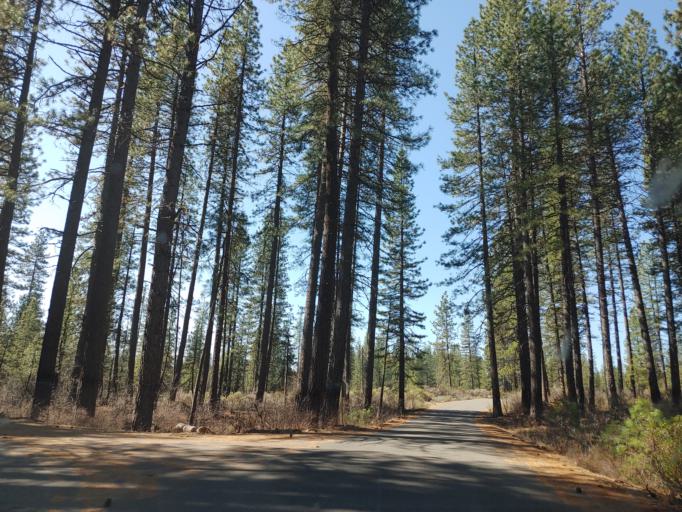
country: US
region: California
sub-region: Siskiyou County
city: McCloud
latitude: 41.2482
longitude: -122.0266
